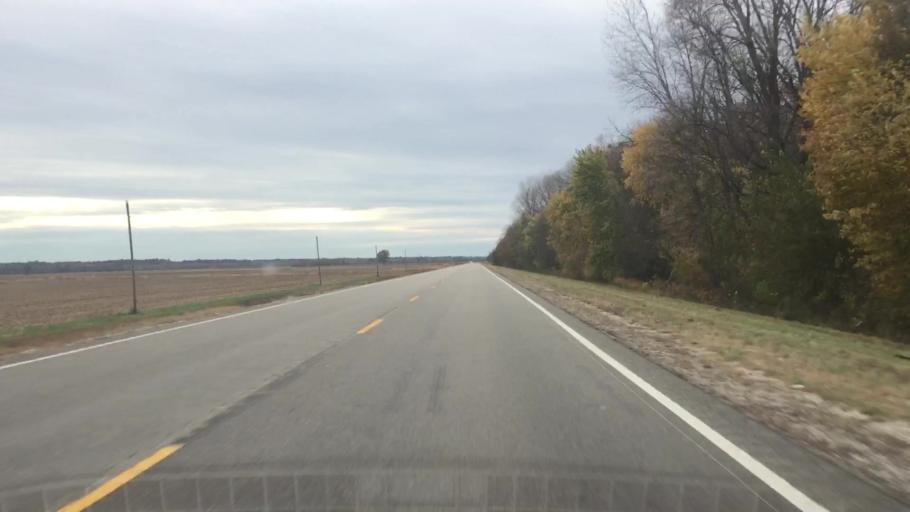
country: US
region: Missouri
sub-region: Callaway County
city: Holts Summit
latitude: 38.5819
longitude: -92.0690
